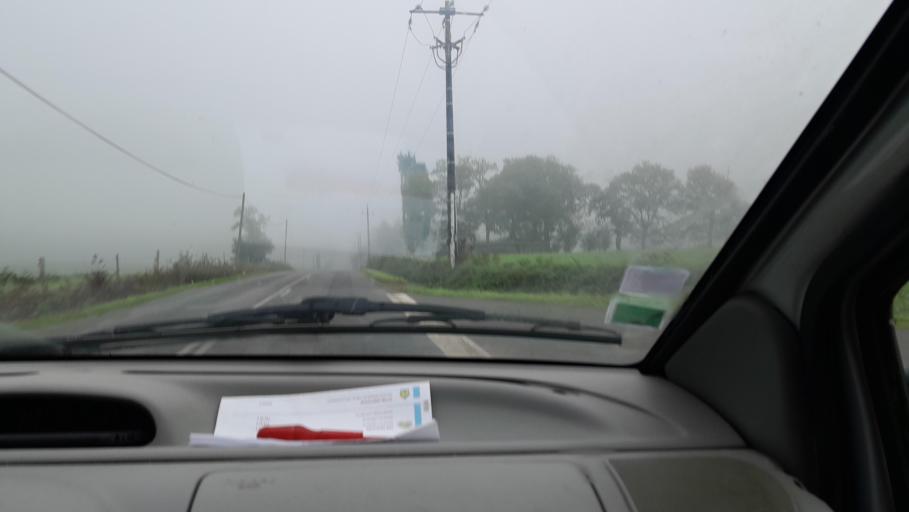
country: FR
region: Brittany
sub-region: Departement d'Ille-et-Vilaine
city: Le Pertre
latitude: 48.0016
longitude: -1.0395
